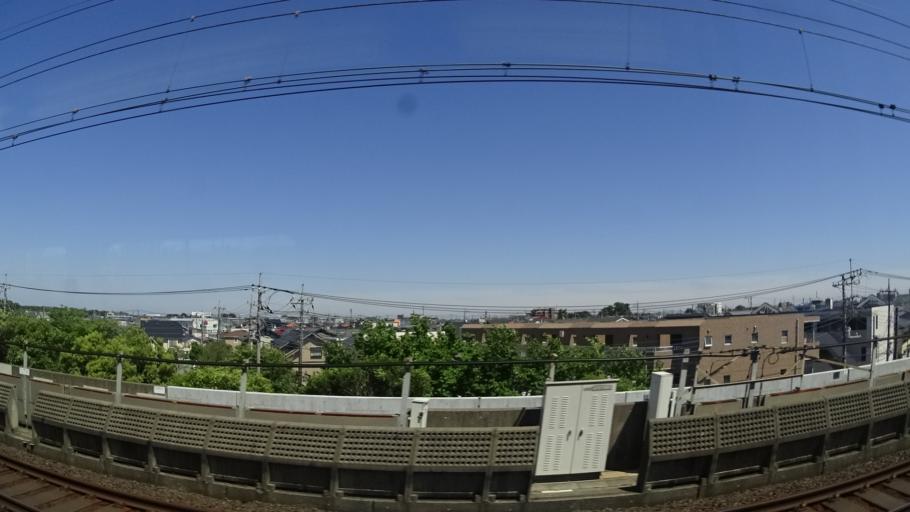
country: JP
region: Saitama
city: Ageoshimo
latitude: 35.9639
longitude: 139.6223
